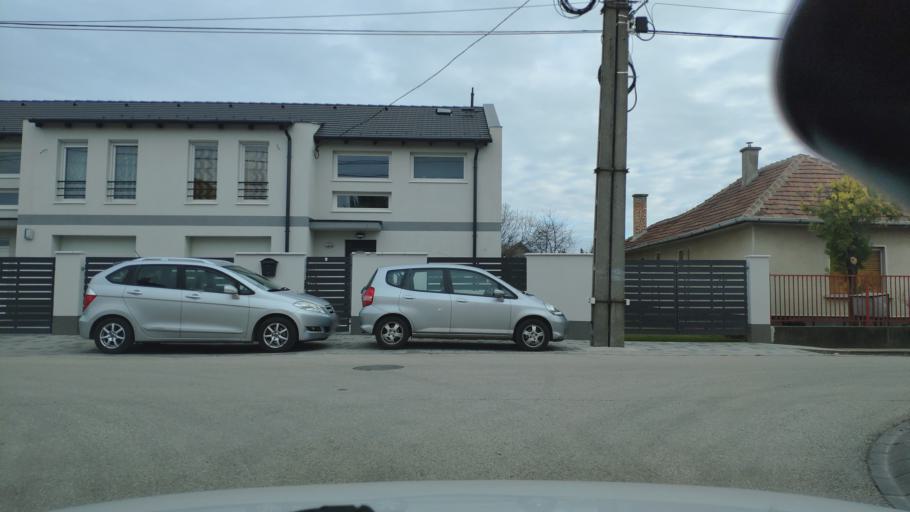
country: HU
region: Pest
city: Dunaharaszti
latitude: 47.3517
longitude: 19.0924
